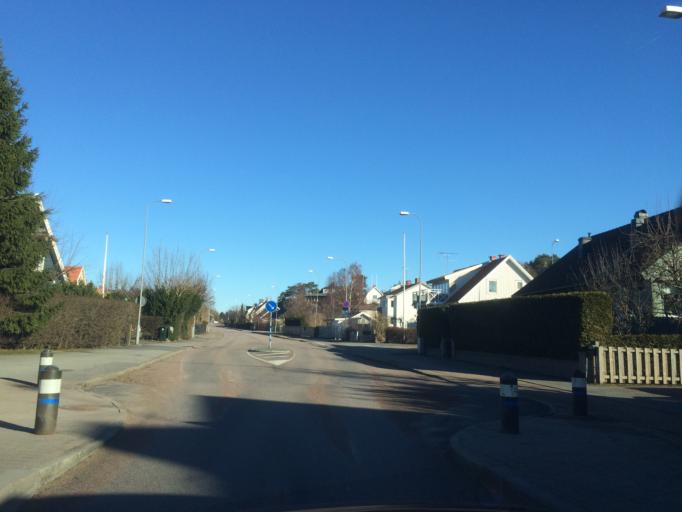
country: SE
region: Vaestra Goetaland
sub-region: Goteborg
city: Majorna
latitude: 57.6698
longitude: 11.8973
